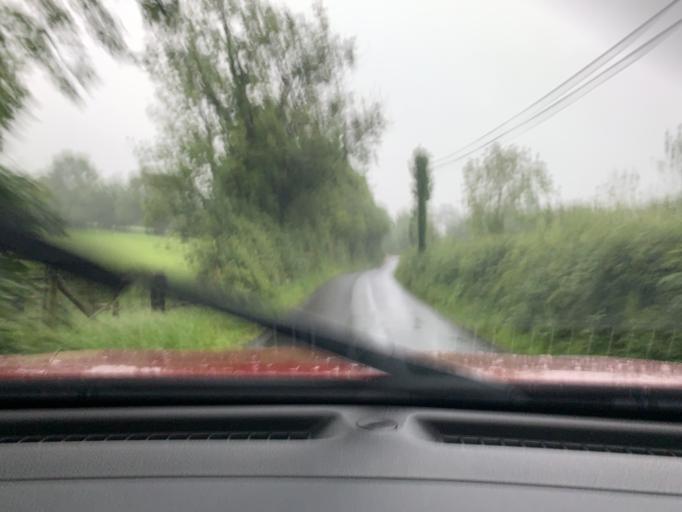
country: IE
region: Connaught
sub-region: Sligo
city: Sligo
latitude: 54.3316
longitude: -8.4148
